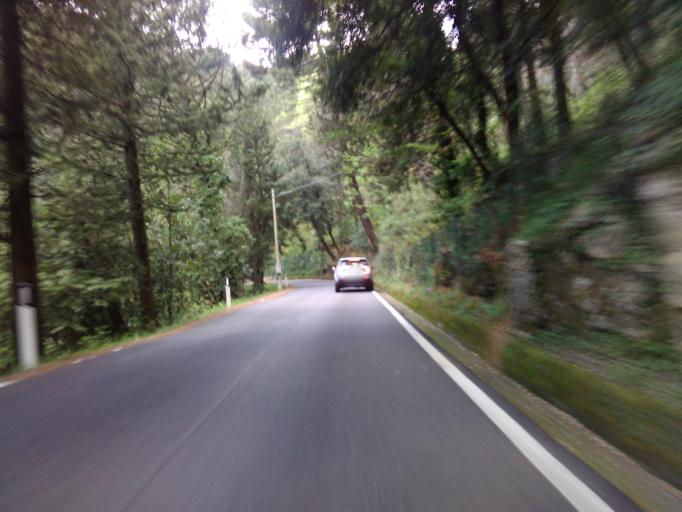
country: IT
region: Tuscany
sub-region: Provincia di Lucca
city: Pontestazzemese
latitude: 43.9557
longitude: 10.2783
